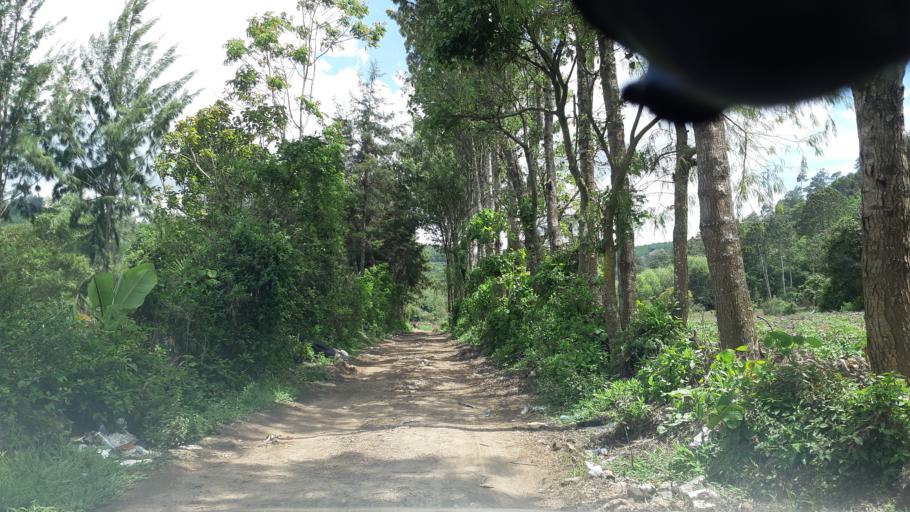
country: GT
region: Chimaltenango
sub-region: Municipio de Chimaltenango
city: Chimaltenango
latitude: 14.6566
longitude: -90.8482
